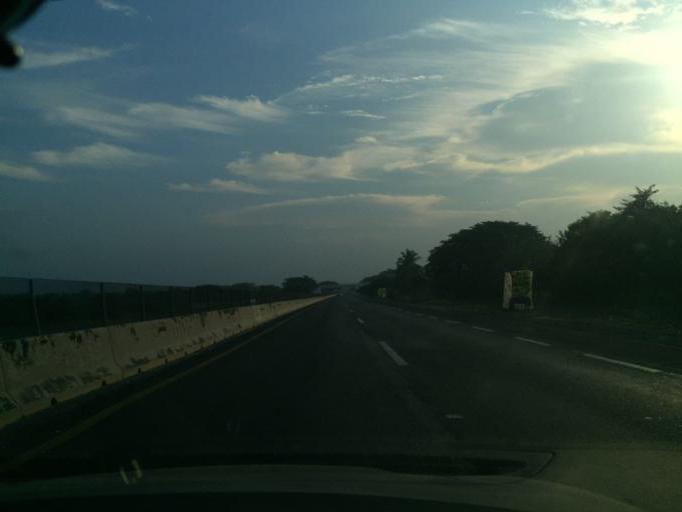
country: MX
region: Veracruz
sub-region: Tierra Blanca
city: Huixcolotla
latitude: 18.7853
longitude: -96.5204
